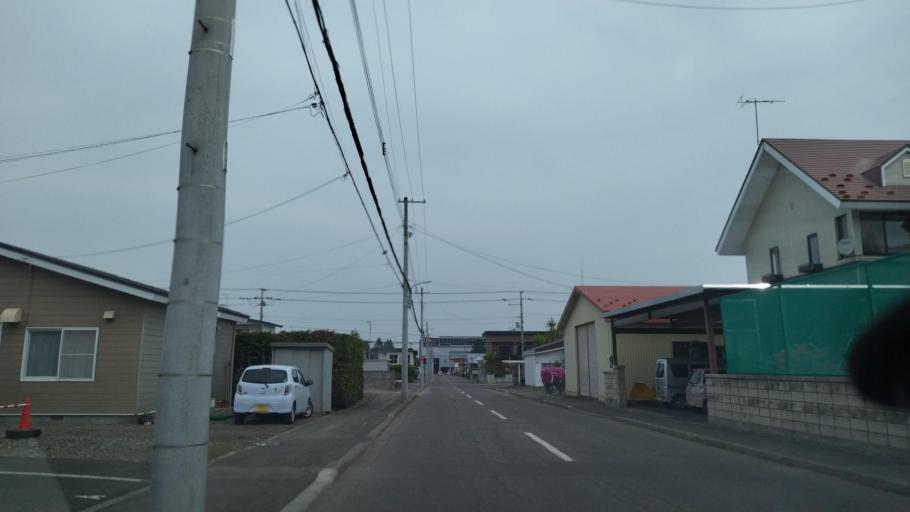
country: JP
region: Hokkaido
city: Obihiro
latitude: 42.9152
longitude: 143.0515
